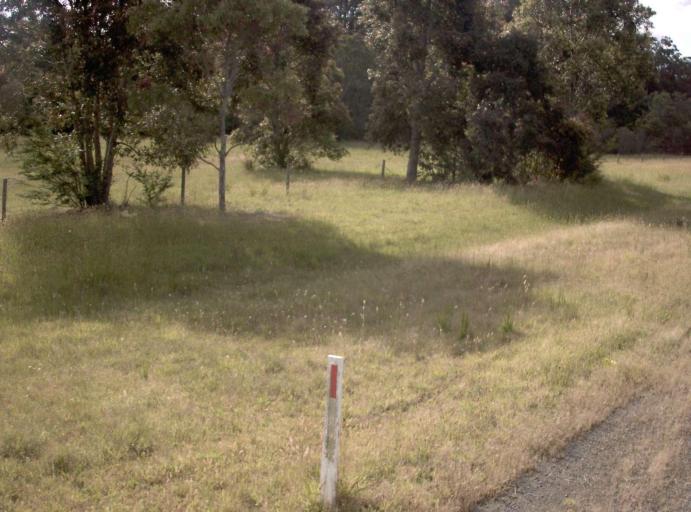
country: AU
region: Victoria
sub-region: Latrobe
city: Moe
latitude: -38.1883
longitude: 146.3297
